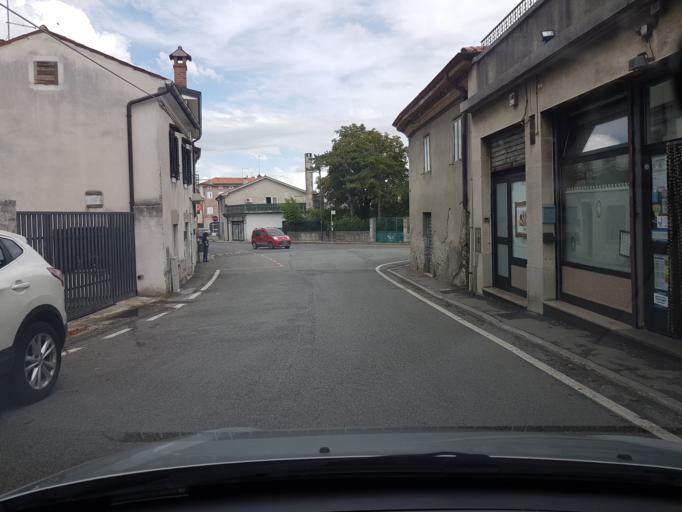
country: IT
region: Friuli Venezia Giulia
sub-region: Provincia di Trieste
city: Prosecco-Contovello
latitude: 45.7073
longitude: 13.7335
